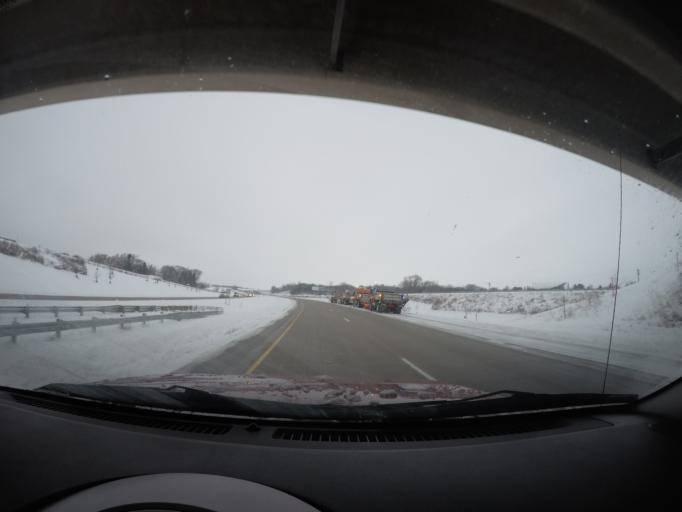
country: US
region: Minnesota
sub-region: Olmsted County
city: Oronoco
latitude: 44.1657
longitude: -92.5453
